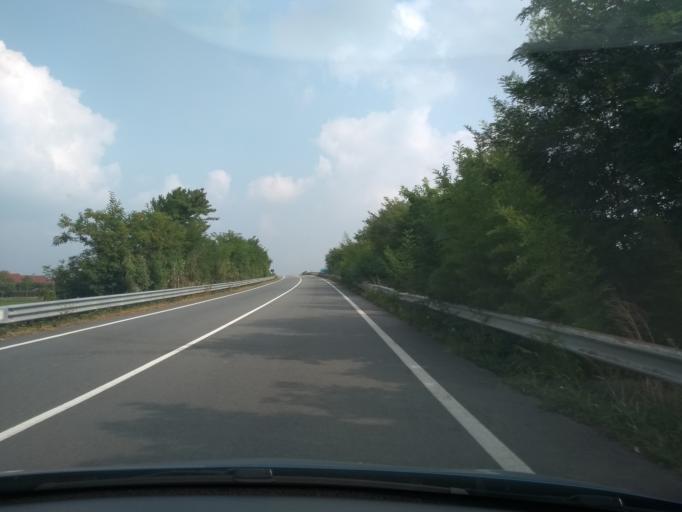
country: IT
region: Piedmont
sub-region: Provincia di Torino
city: Castellamonte
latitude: 45.3637
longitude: 7.7222
